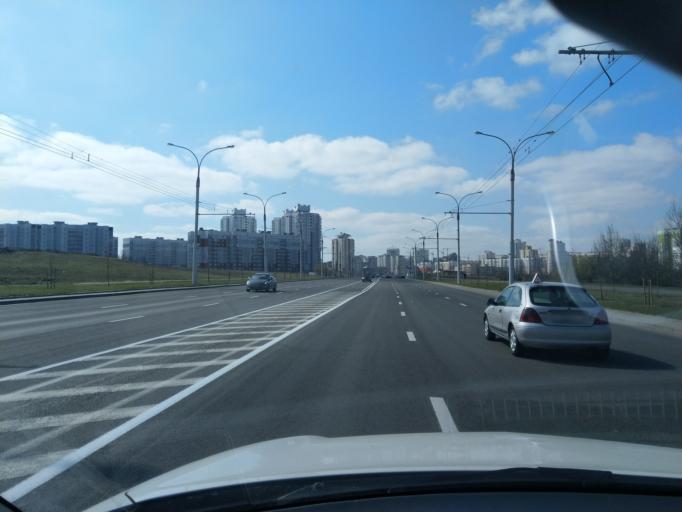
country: BY
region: Minsk
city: Yubilyeyny
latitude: 53.8549
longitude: 27.4958
